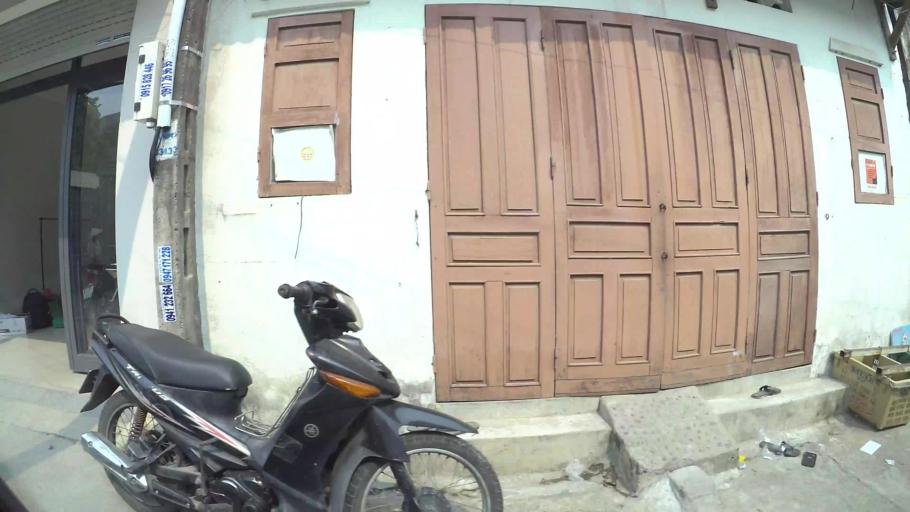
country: VN
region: Da Nang
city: Son Tra
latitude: 16.0424
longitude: 108.2172
